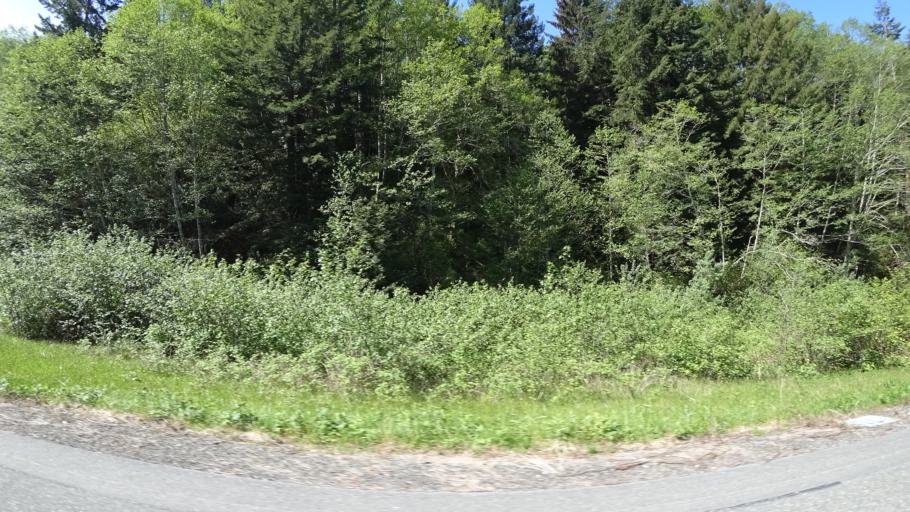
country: US
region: California
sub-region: Del Norte County
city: Bertsch-Oceanview
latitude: 41.4652
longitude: -124.0381
